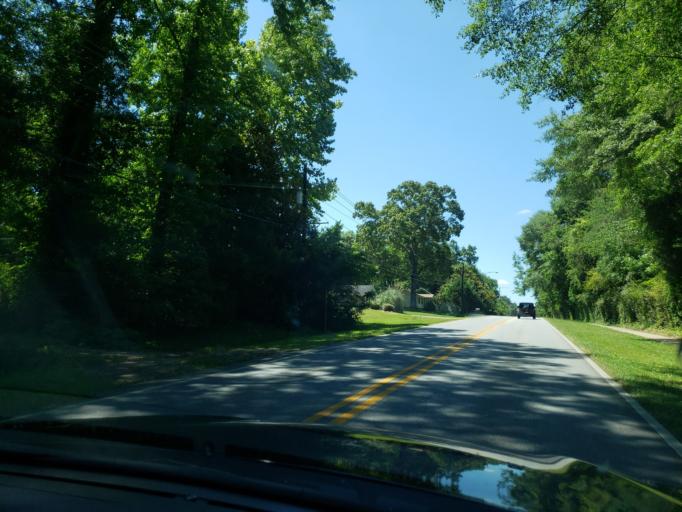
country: US
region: Alabama
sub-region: Lee County
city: Auburn
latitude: 32.6218
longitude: -85.4819
